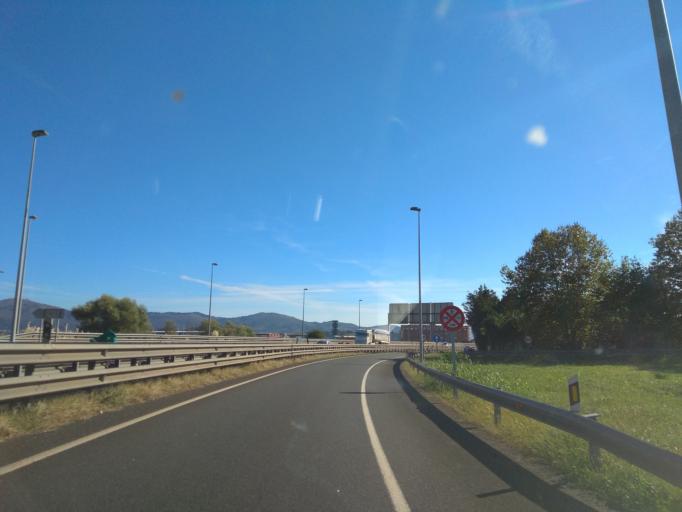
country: ES
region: Cantabria
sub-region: Provincia de Cantabria
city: Santander
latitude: 43.4385
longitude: -3.8330
